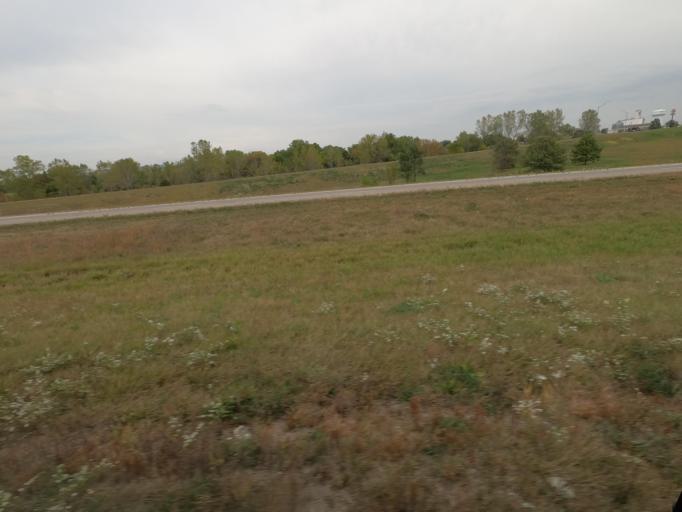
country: US
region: Iowa
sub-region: Marion County
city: Pella
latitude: 41.3892
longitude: -92.9151
